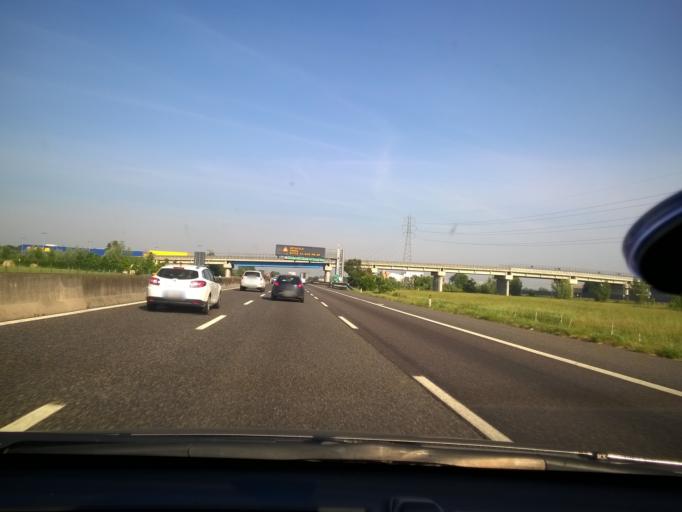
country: IT
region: Emilia-Romagna
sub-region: Provincia di Parma
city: Parma
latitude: 44.8302
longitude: 10.3697
